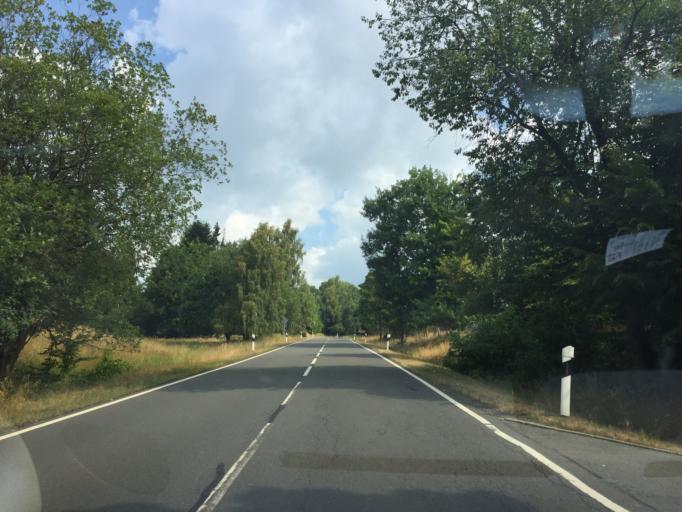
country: DE
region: Lower Saxony
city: Zorge
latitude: 51.6545
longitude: 10.6607
